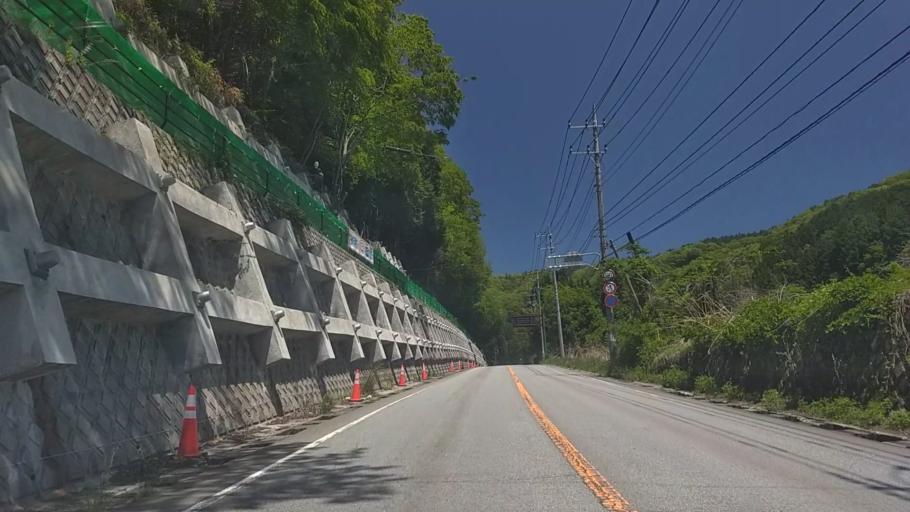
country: JP
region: Yamanashi
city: Nirasaki
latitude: 35.8822
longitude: 138.4263
